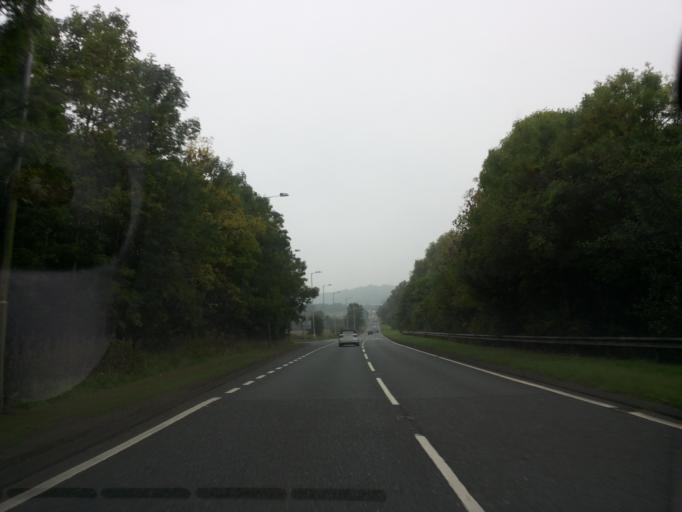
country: GB
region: England
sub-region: Lancashire
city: Longridge
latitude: 53.7655
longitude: -2.6222
